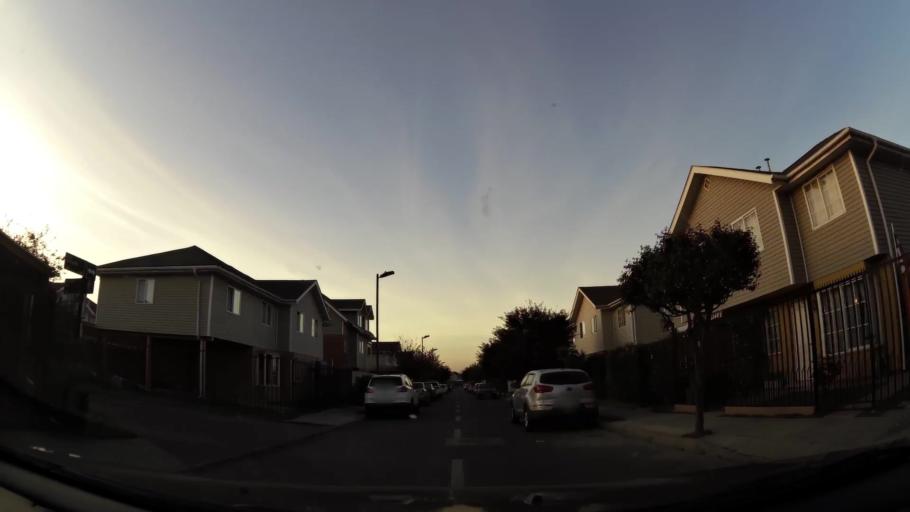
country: CL
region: Santiago Metropolitan
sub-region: Provincia de Cordillera
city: Puente Alto
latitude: -33.5980
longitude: -70.5853
